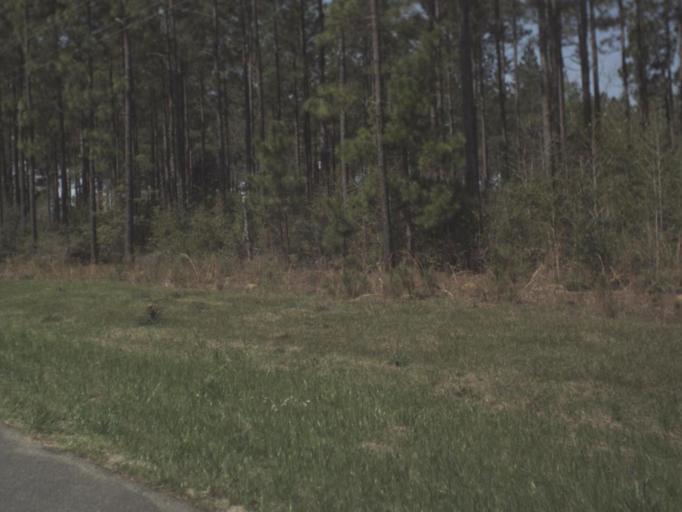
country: US
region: Alabama
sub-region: Geneva County
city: Geneva
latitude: 30.9488
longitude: -85.9360
